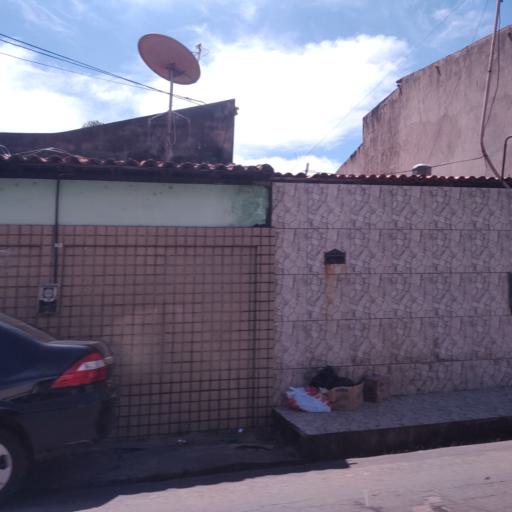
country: BR
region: Maranhao
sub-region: Sao Luis
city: Sao Luis
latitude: -2.5396
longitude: -44.2788
